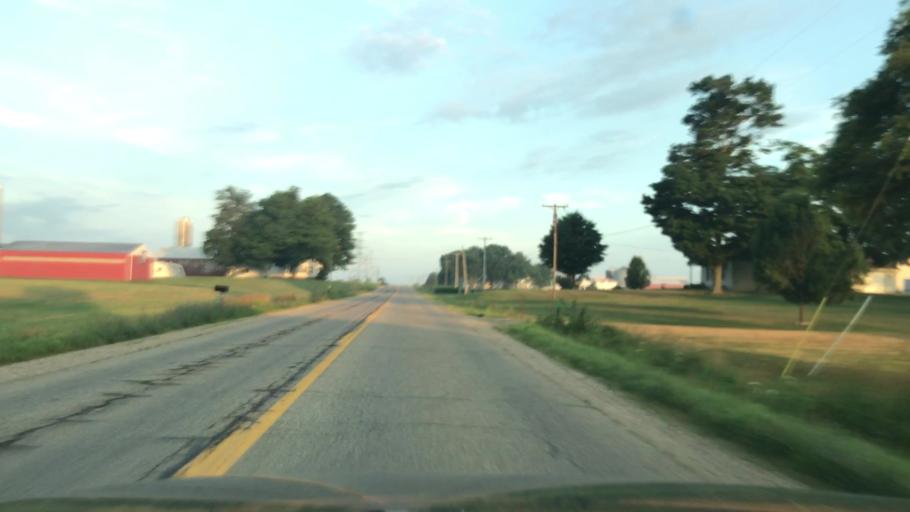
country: US
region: Michigan
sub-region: Ottawa County
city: Hudsonville
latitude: 42.7823
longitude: -85.8964
